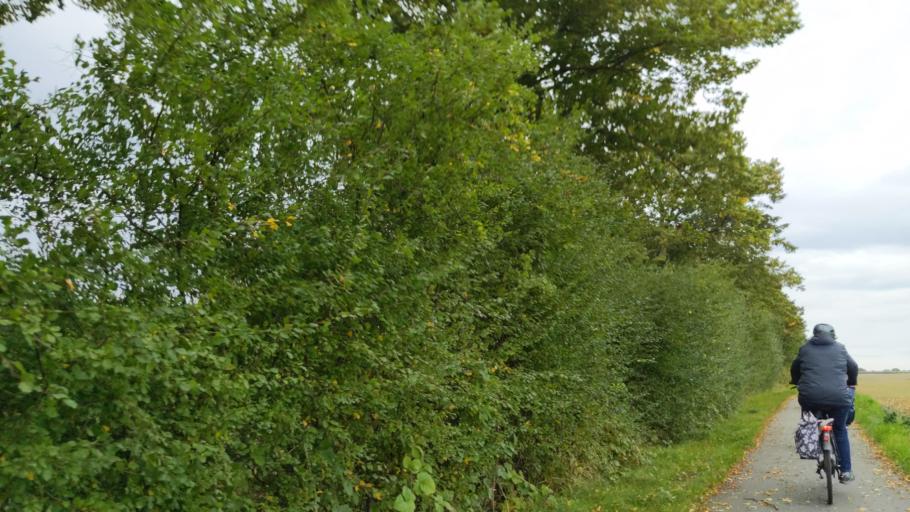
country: DE
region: Mecklenburg-Vorpommern
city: Schlagsdorf
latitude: 53.7623
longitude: 10.8126
